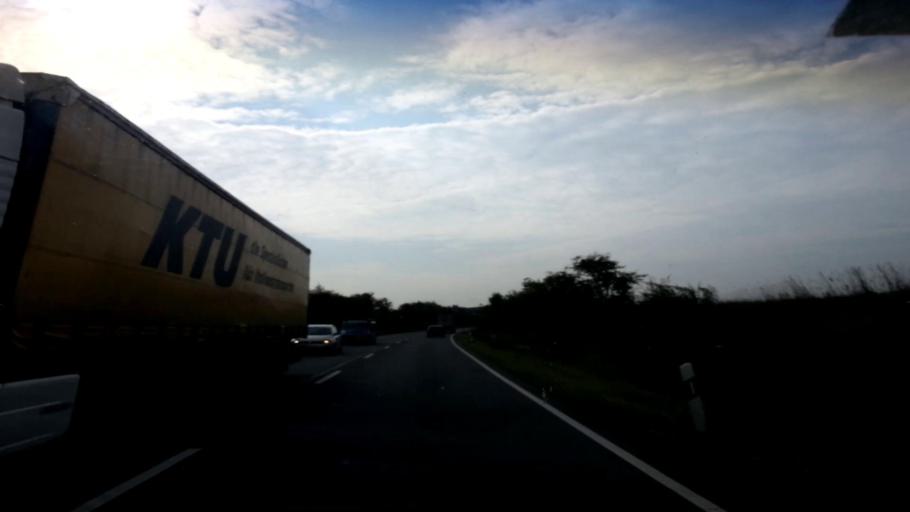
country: DE
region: Bavaria
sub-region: Regierungsbezirk Unterfranken
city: Prichsenstadt
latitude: 49.8407
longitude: 10.3524
